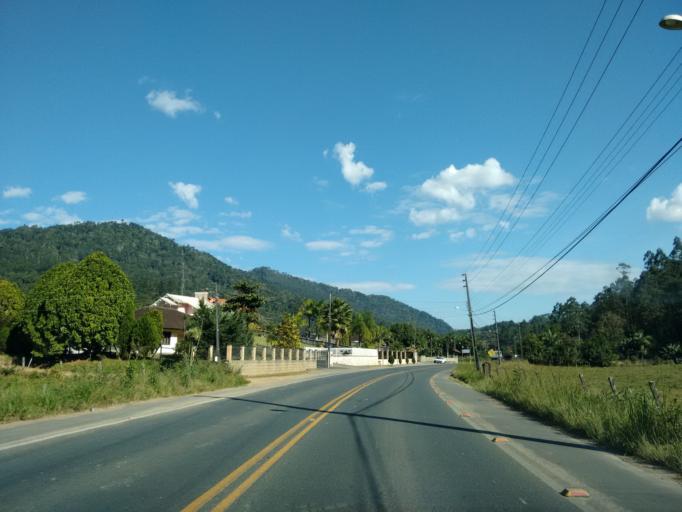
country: BR
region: Santa Catarina
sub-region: Pomerode
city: Pomerode
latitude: -26.7390
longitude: -49.2174
